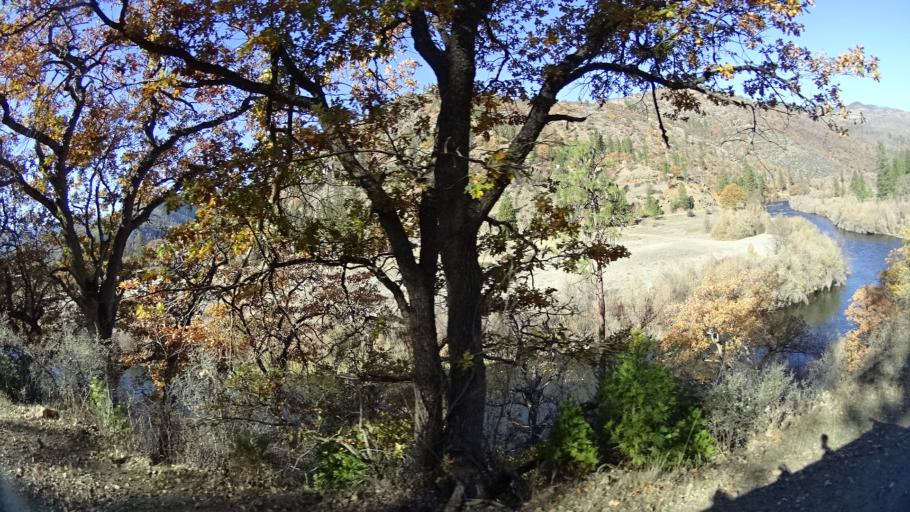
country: US
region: California
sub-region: Siskiyou County
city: Yreka
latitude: 41.8385
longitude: -122.8358
